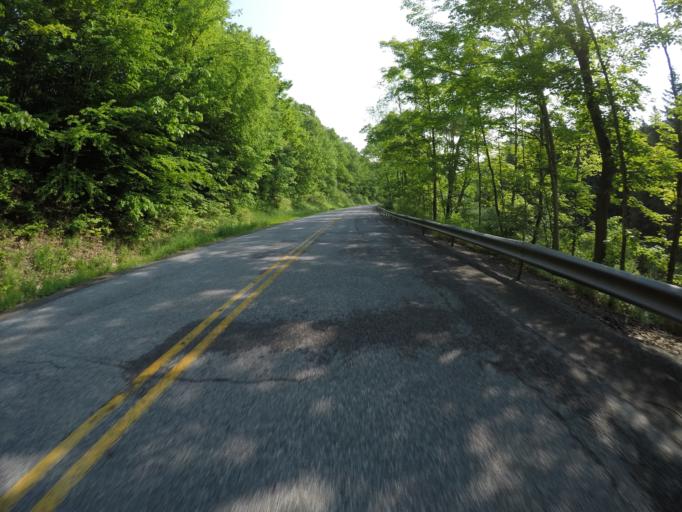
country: US
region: New York
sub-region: Sullivan County
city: Livingston Manor
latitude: 42.1290
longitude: -74.6728
